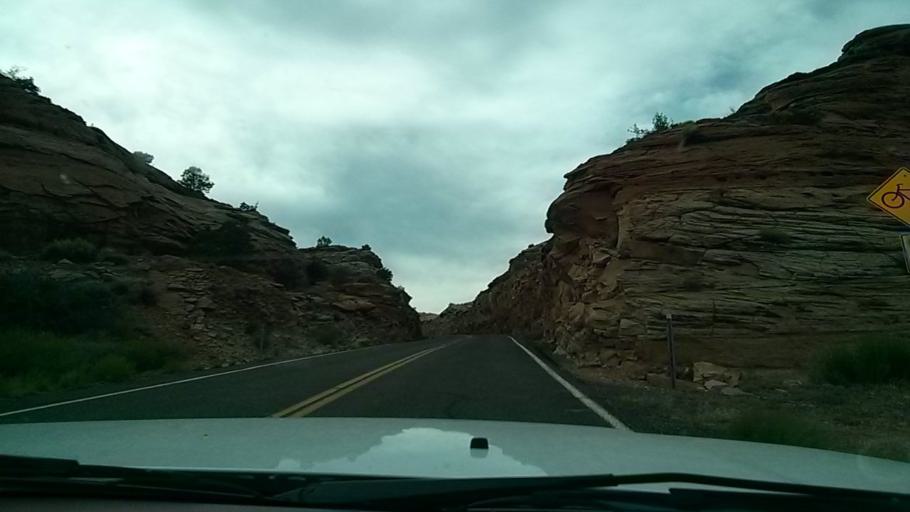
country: US
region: Utah
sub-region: Wayne County
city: Loa
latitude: 37.7722
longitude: -111.4195
